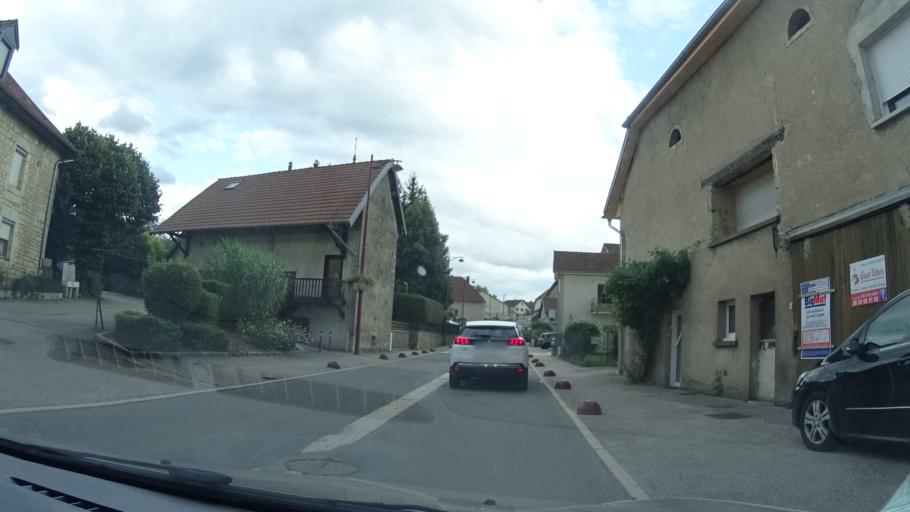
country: FR
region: Franche-Comte
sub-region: Departement du Doubs
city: Saone
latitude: 47.2260
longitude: 6.1165
